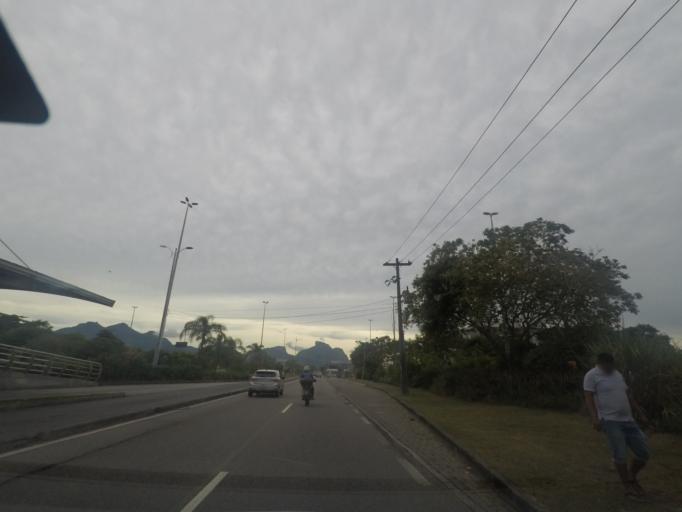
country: BR
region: Rio de Janeiro
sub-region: Rio De Janeiro
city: Rio de Janeiro
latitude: -23.0004
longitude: -43.3773
